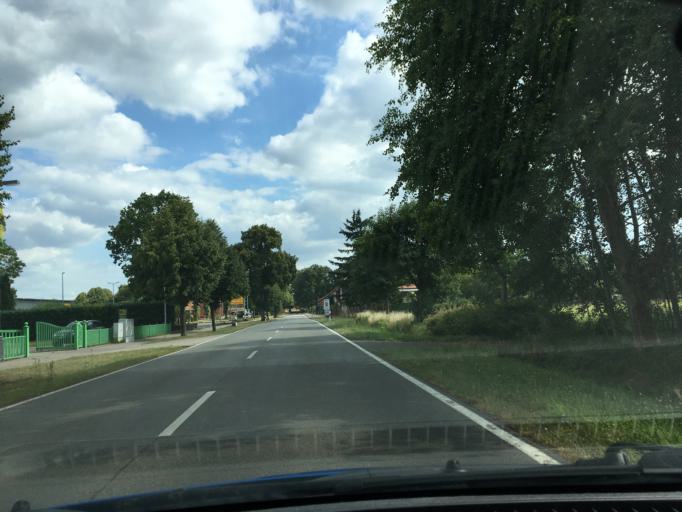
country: DE
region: Mecklenburg-Vorpommern
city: Lubtheen
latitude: 53.3109
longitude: 11.0779
